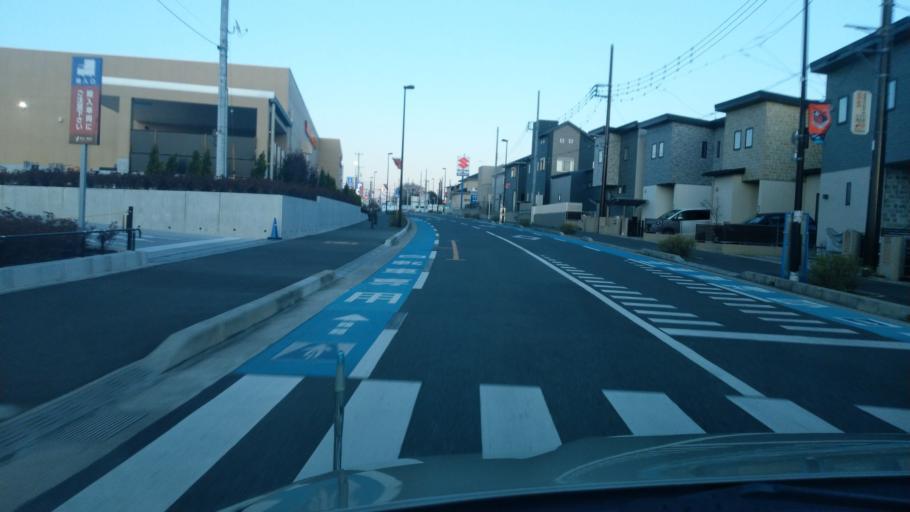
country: JP
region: Saitama
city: Ageoshimo
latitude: 35.9307
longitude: 139.5781
